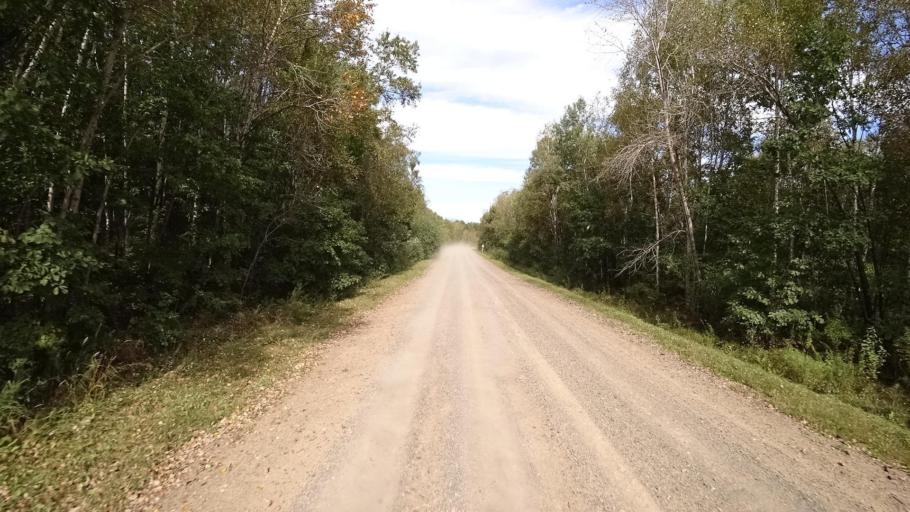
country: RU
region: Primorskiy
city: Yakovlevka
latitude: 44.6753
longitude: 133.6124
